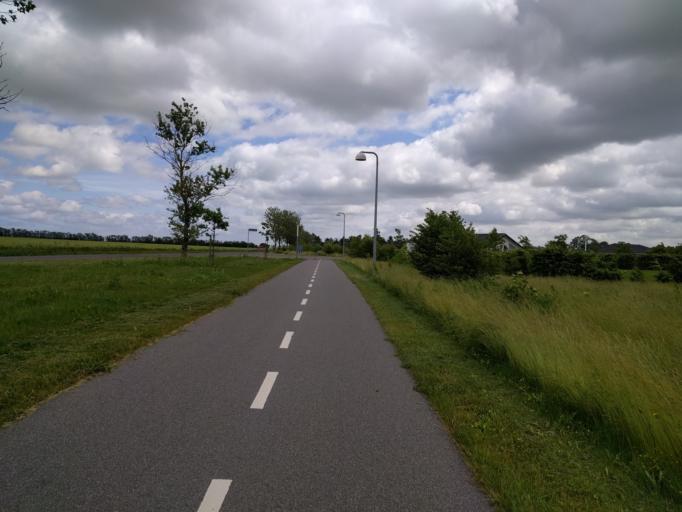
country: DK
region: South Denmark
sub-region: Odense Kommune
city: Bullerup
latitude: 55.4098
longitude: 10.4595
